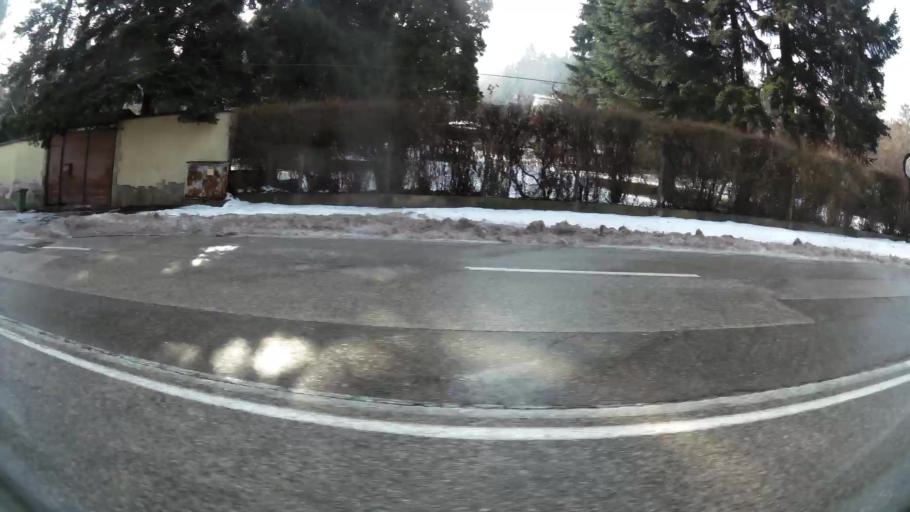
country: BG
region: Sofia-Capital
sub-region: Stolichna Obshtina
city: Sofia
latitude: 42.6490
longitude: 23.2520
